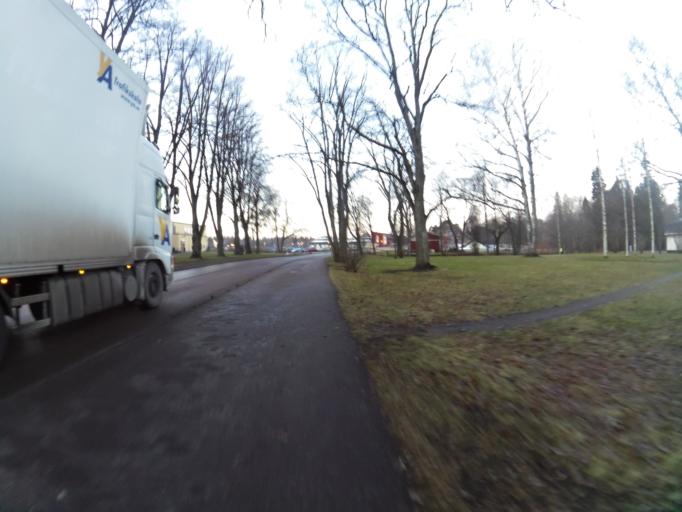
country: SE
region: Gaevleborg
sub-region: Gavle Kommun
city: Gavle
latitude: 60.6689
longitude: 17.1177
